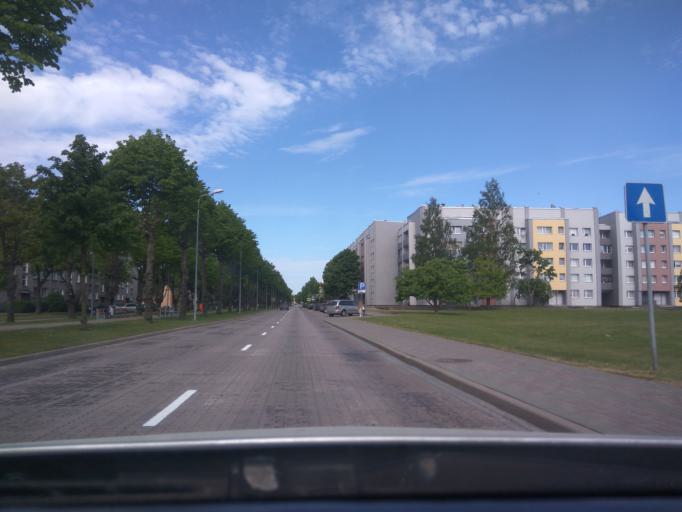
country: LV
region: Ventspils
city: Ventspils
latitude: 57.3906
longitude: 21.5810
